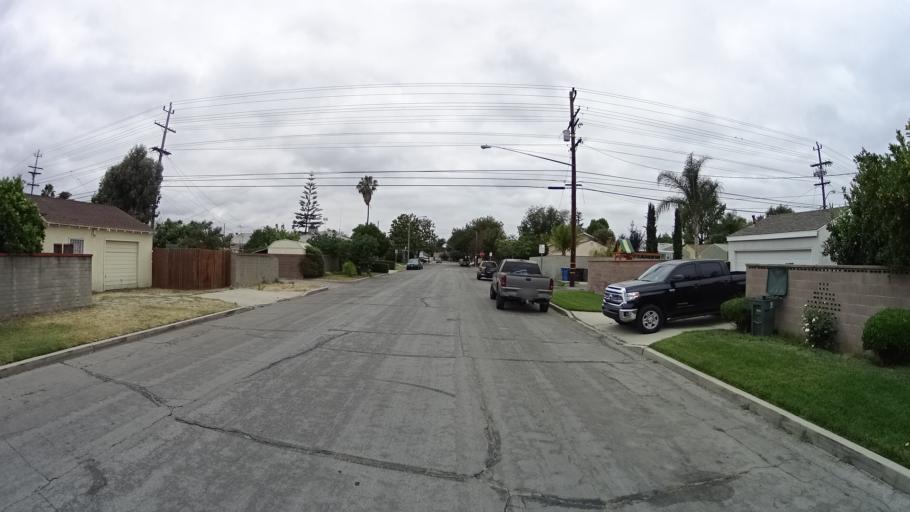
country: US
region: California
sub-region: Los Angeles County
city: Burbank
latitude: 34.1827
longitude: -118.3362
